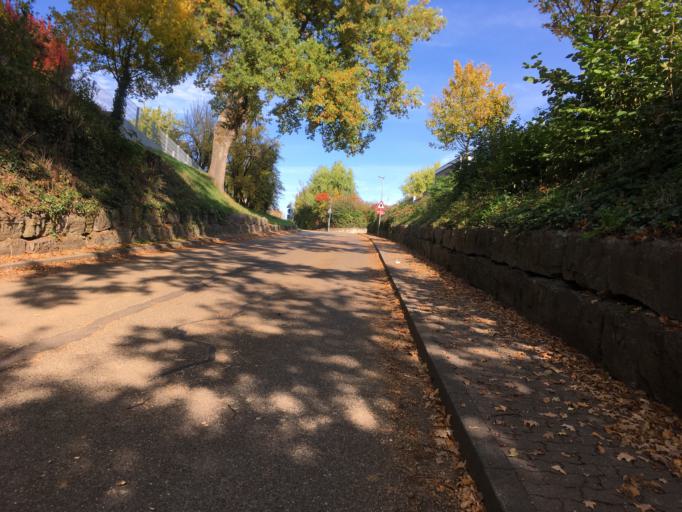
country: DE
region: Baden-Wuerttemberg
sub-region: Regierungsbezirk Stuttgart
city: Siegelsbach
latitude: 49.2584
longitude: 9.0396
